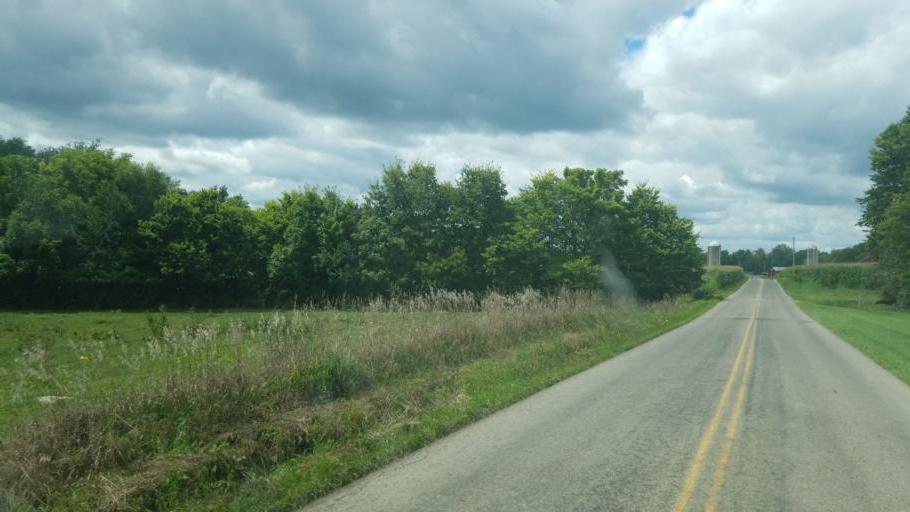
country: US
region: Ohio
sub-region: Knox County
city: Fredericktown
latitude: 40.5419
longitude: -82.6038
